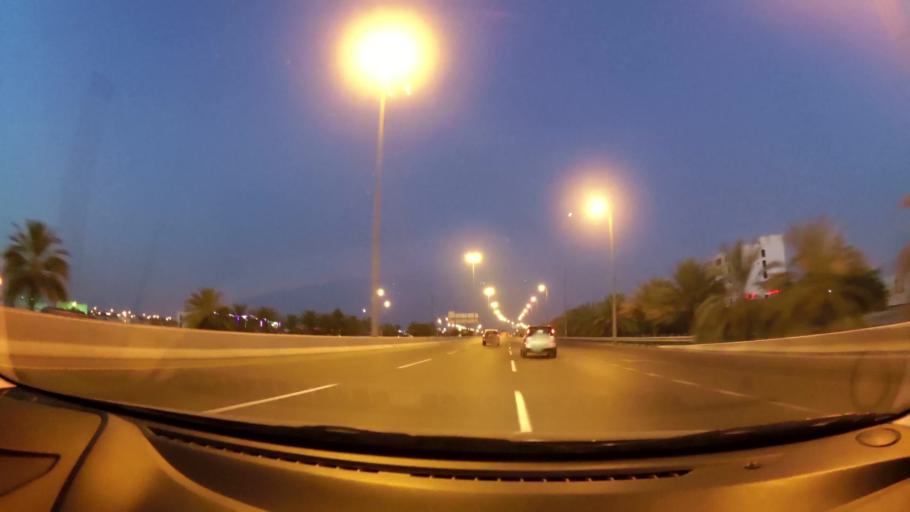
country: OM
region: Muhafazat Masqat
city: As Sib al Jadidah
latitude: 23.6568
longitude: 58.1969
